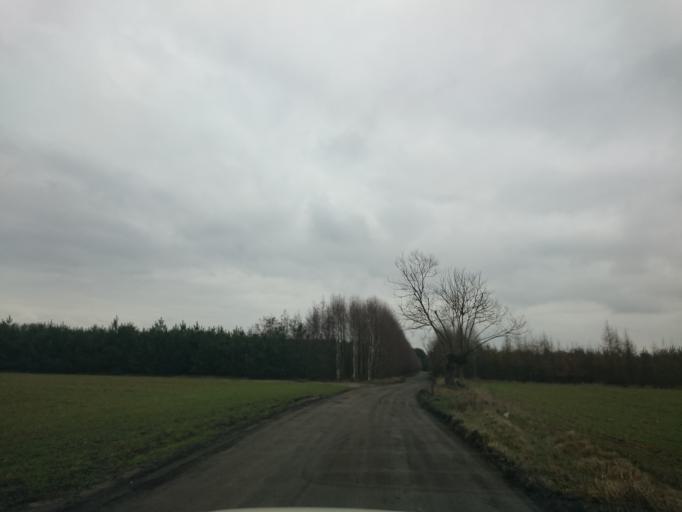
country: PL
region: Kujawsko-Pomorskie
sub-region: Powiat golubsko-dobrzynski
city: Ciechocin
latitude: 53.0506
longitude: 18.8490
